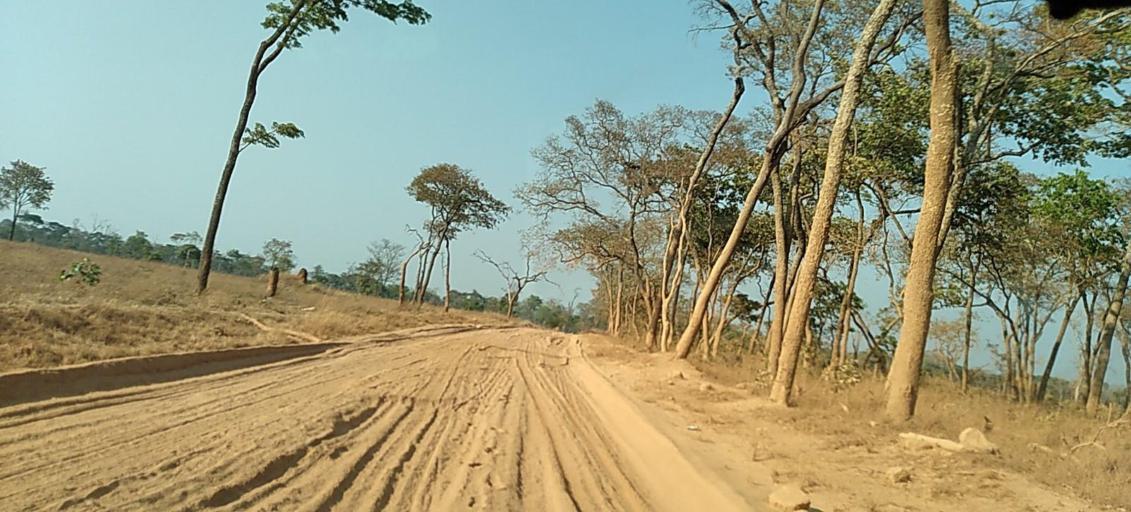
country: ZM
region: North-Western
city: Kasempa
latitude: -13.5699
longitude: 25.9946
